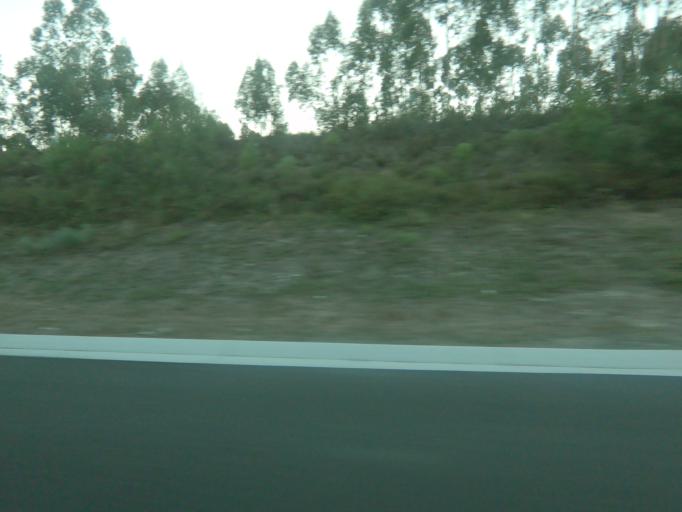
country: PT
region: Leiria
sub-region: Pombal
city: Pombal
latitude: 39.8744
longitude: -8.7021
